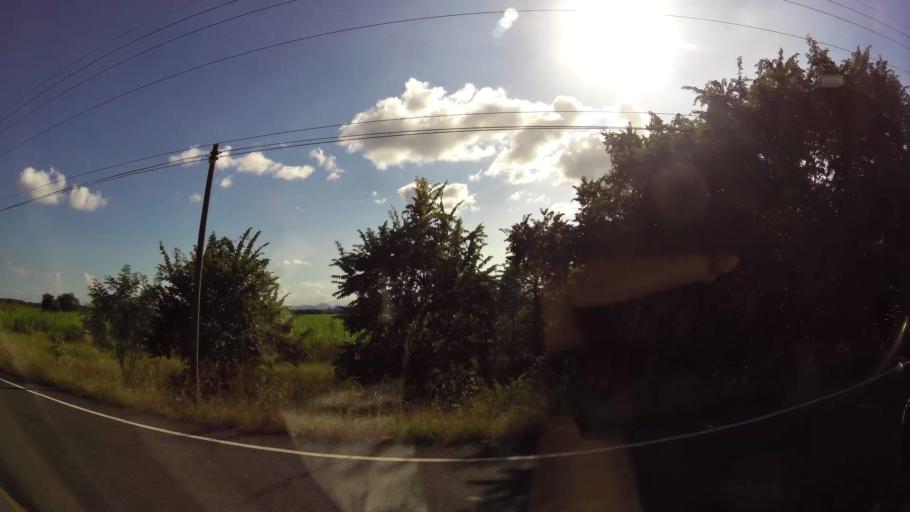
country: CR
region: Guanacaste
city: Sardinal
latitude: 10.5700
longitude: -85.6198
